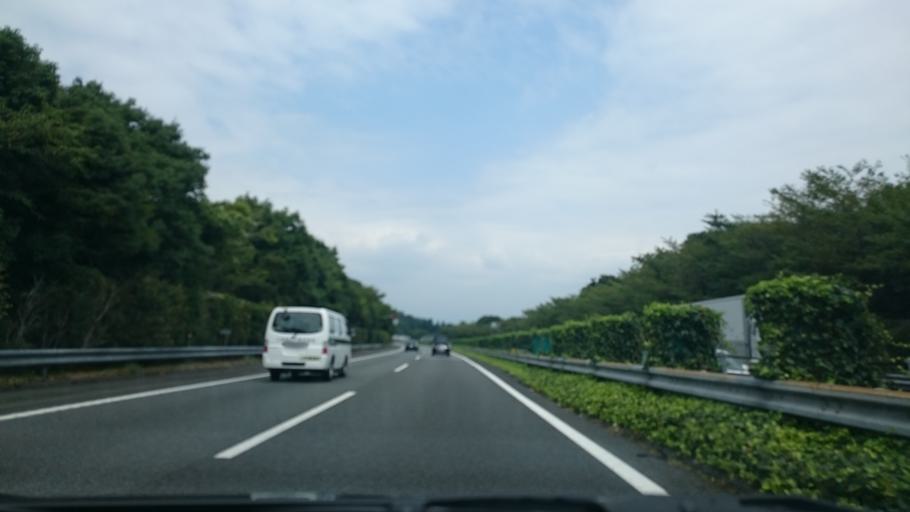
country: JP
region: Shizuoka
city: Fuji
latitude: 35.1331
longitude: 138.6145
